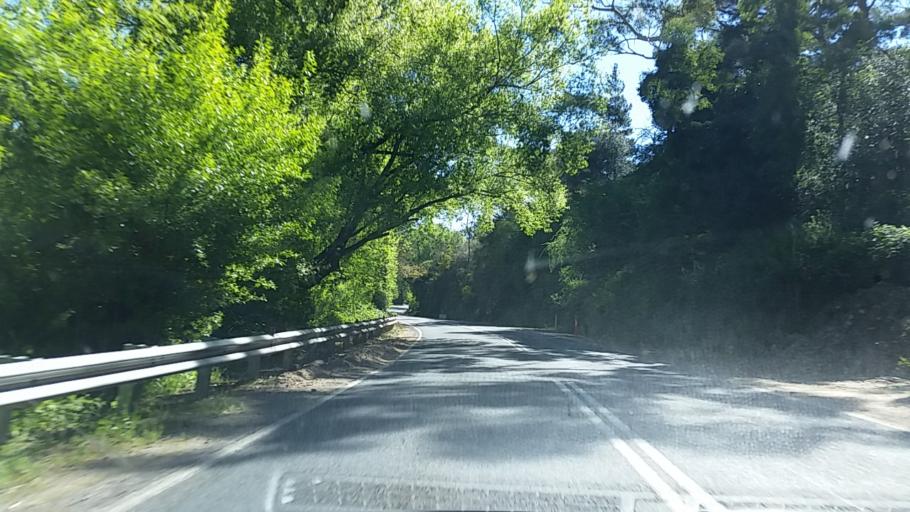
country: AU
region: South Australia
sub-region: Mount Barker
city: Meadows
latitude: -35.1619
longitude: 138.6935
